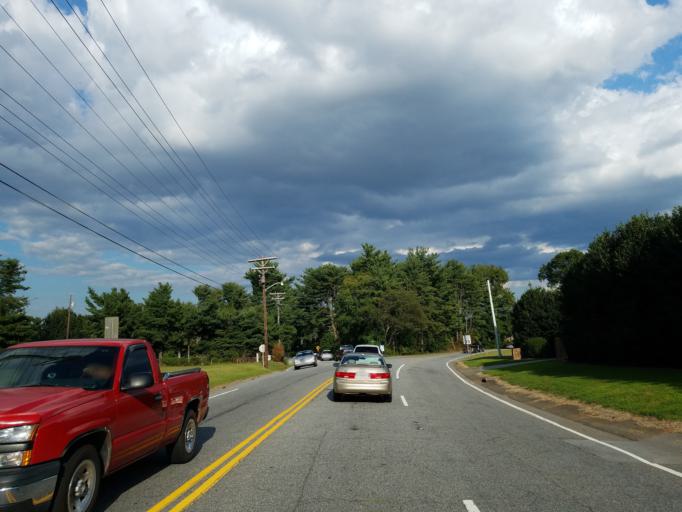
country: US
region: South Carolina
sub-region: Greenville County
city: Wade Hampton
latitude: 34.8463
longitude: -82.3026
